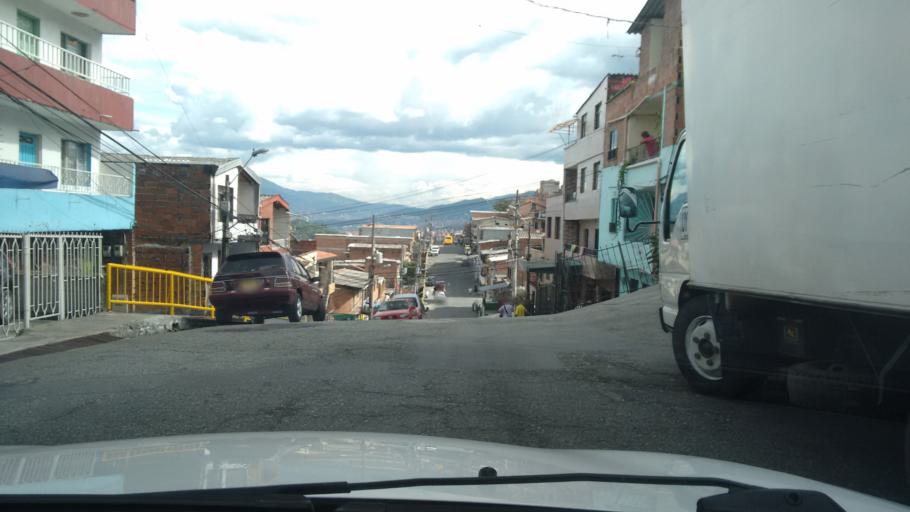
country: CO
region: Antioquia
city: Medellin
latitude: 6.2958
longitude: -75.5796
